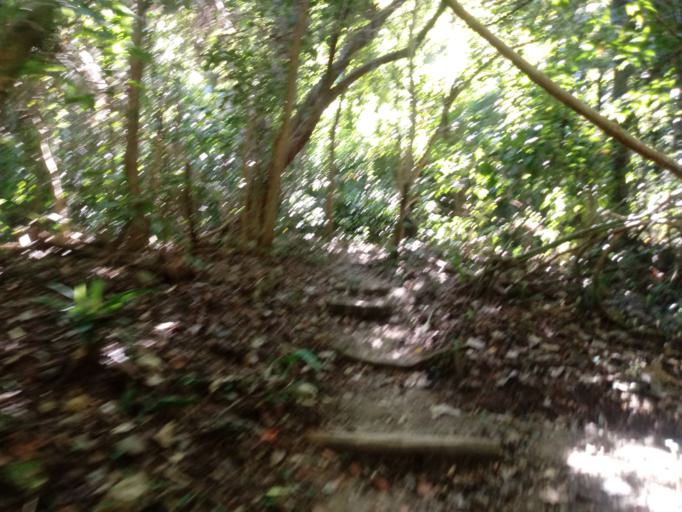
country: CR
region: Puntarenas
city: Paquera
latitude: 9.5860
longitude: -85.0985
